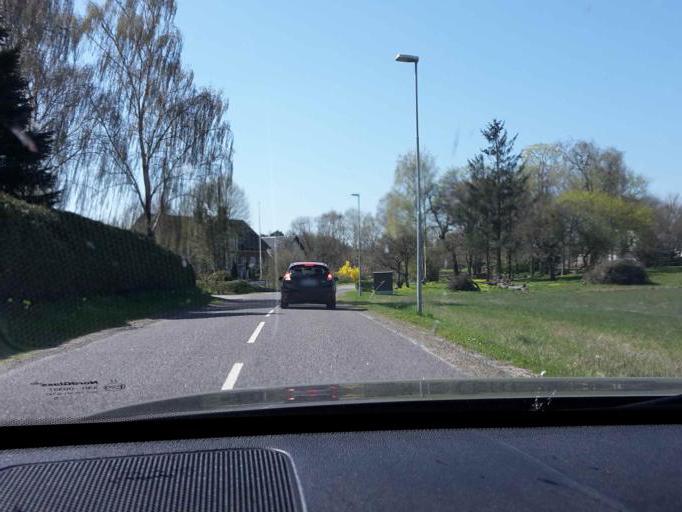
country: DK
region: South Denmark
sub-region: Odense Kommune
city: Bellinge
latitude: 55.3815
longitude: 10.3113
